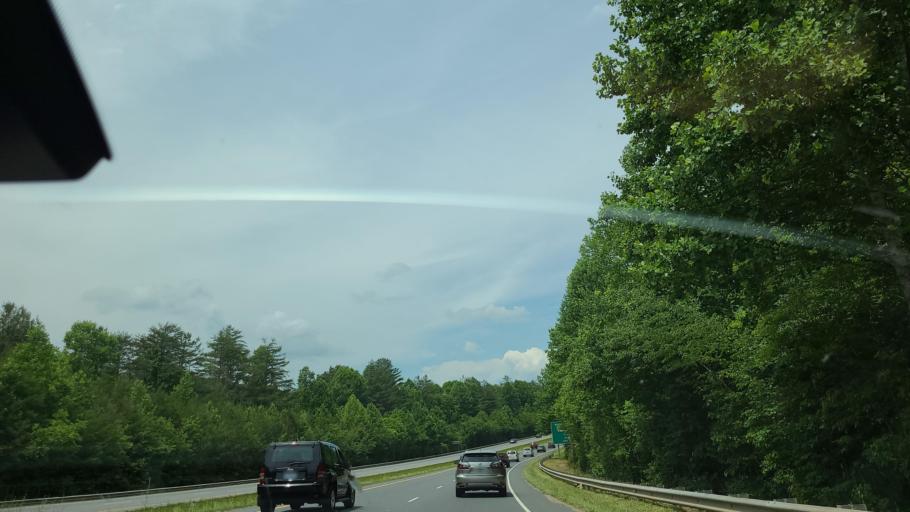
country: US
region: North Carolina
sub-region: Macon County
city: Franklin
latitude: 35.1641
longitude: -83.3766
